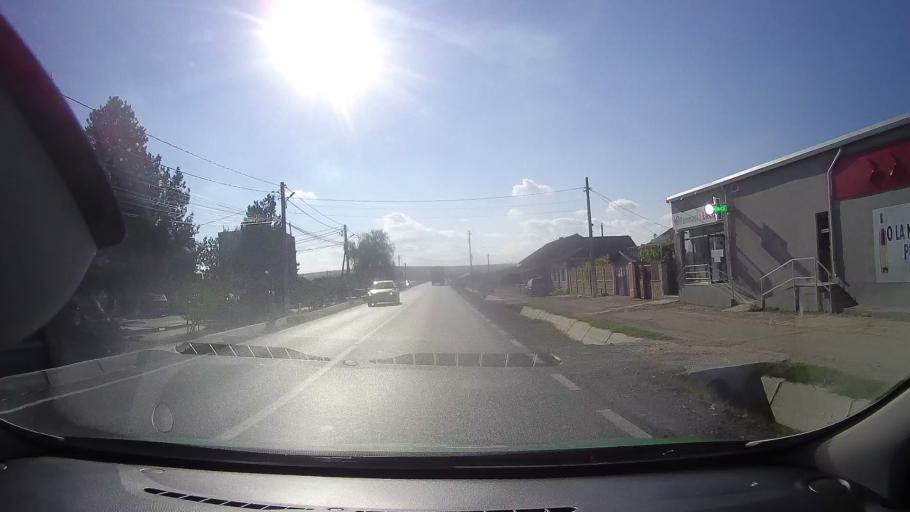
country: RO
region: Tulcea
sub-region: Comuna Baia
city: Baia
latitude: 44.7254
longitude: 28.6802
